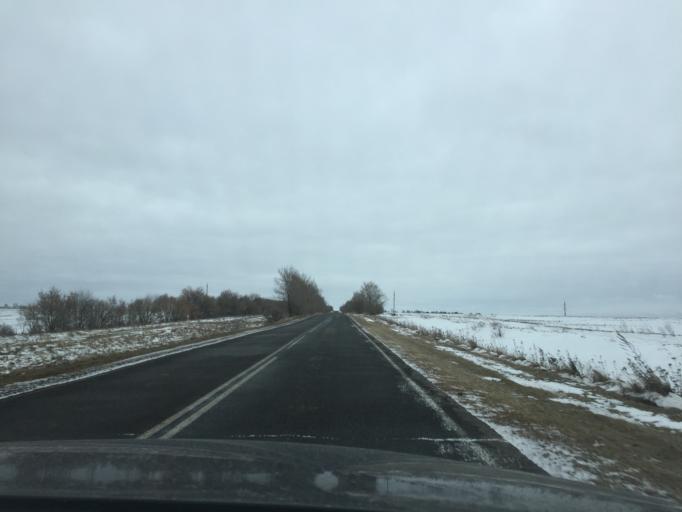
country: RU
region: Tula
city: Shchekino
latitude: 53.8255
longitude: 37.5183
